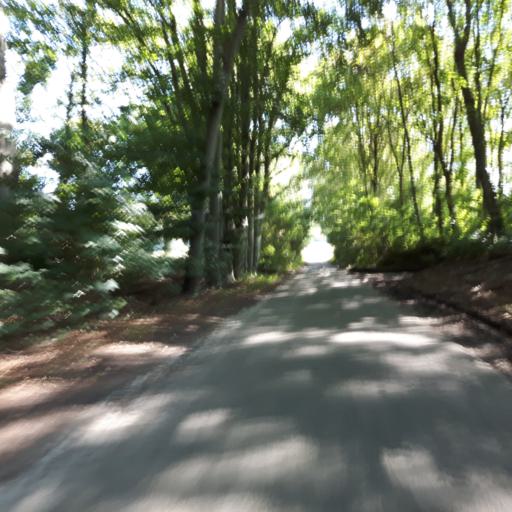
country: NL
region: North Brabant
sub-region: Gemeente Woensdrecht
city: Woensdrecht
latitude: 51.4599
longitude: 4.3020
